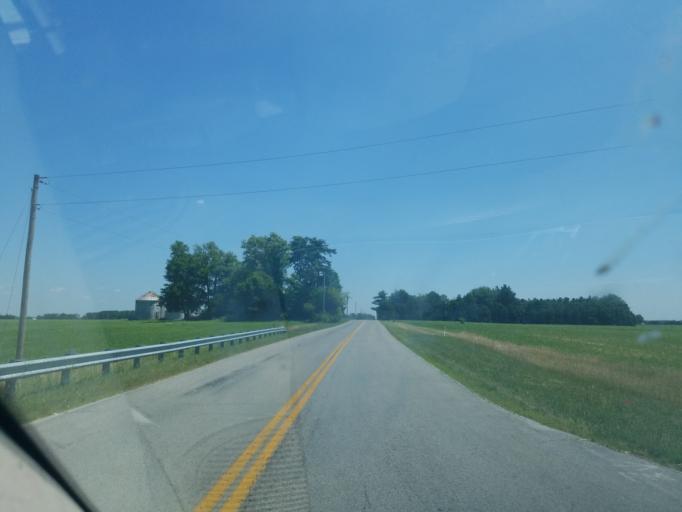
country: US
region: Ohio
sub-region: Allen County
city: Delphos
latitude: 40.7868
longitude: -84.2899
